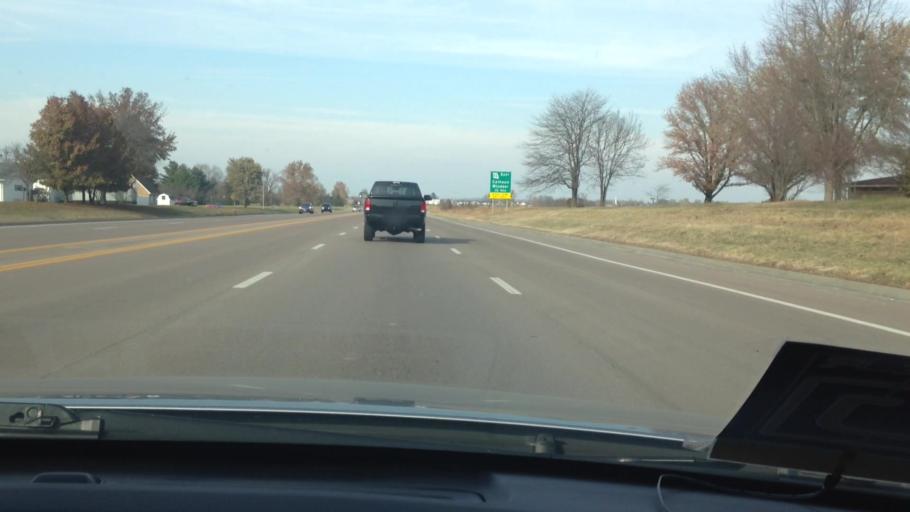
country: US
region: Missouri
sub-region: Henry County
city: Clinton
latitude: 38.3725
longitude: -93.7518
